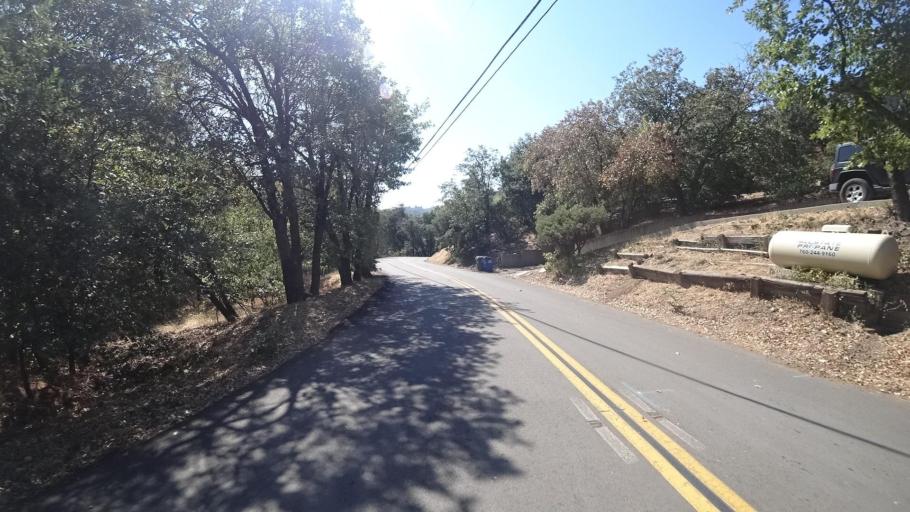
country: US
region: California
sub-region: San Diego County
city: Julian
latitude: 33.0633
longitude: -116.5755
